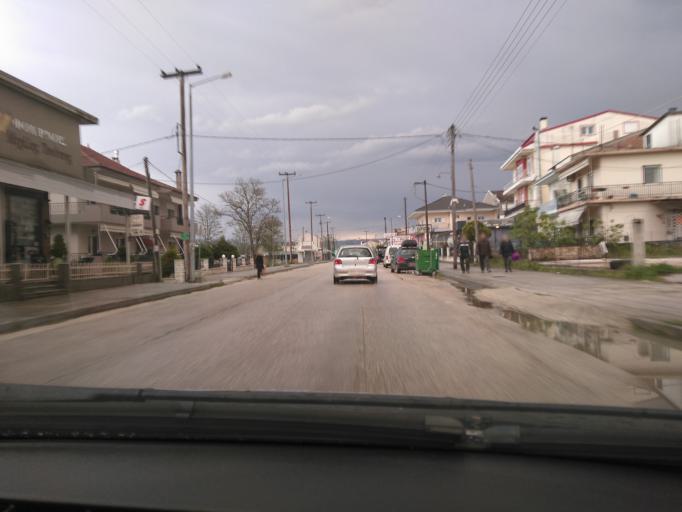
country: GR
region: Epirus
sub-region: Nomos Ioanninon
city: Anatoli
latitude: 39.6379
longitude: 20.8698
